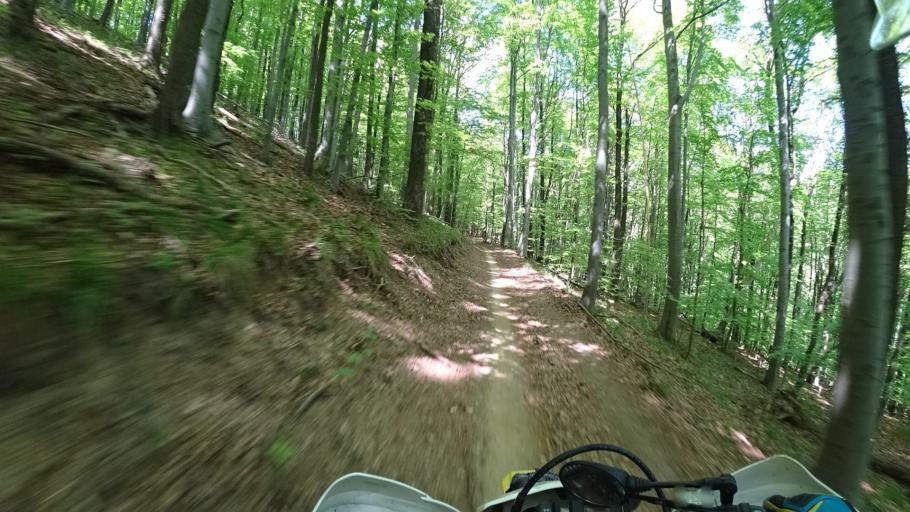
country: HR
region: Zagrebacka
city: Jablanovec
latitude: 45.8799
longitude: 15.9008
